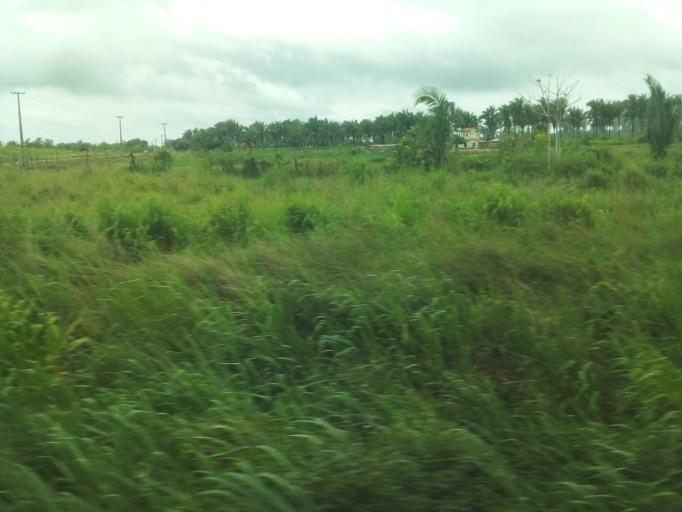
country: BR
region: Maranhao
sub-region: Moncao
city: Moncao
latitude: -3.6288
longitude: -45.1916
